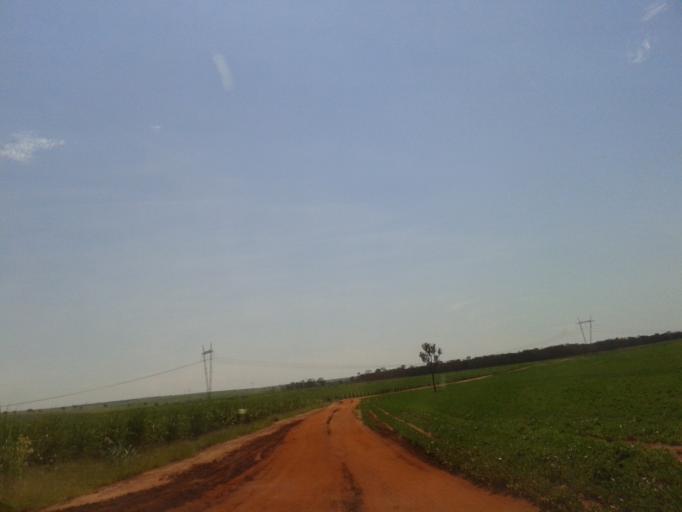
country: BR
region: Minas Gerais
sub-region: Santa Vitoria
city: Santa Vitoria
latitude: -19.0646
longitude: -50.4717
